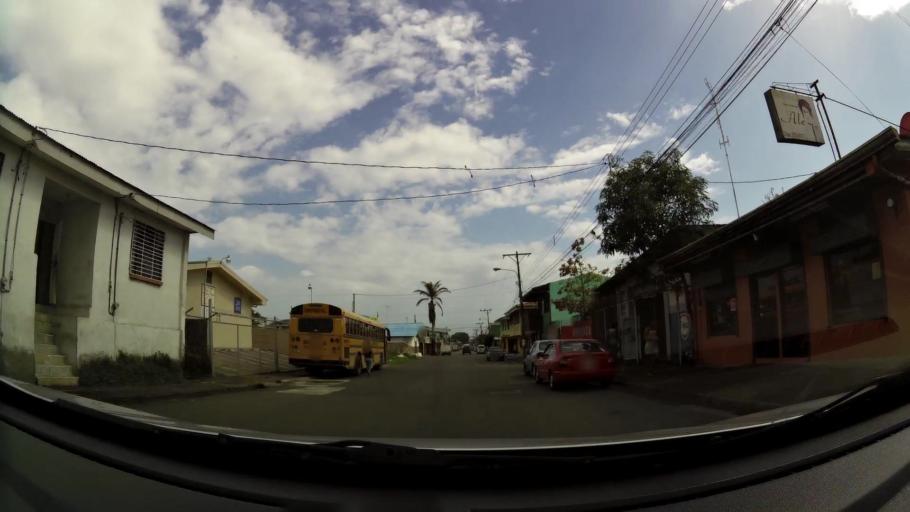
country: CR
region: Limon
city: Limon
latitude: 9.9935
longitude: -83.0341
